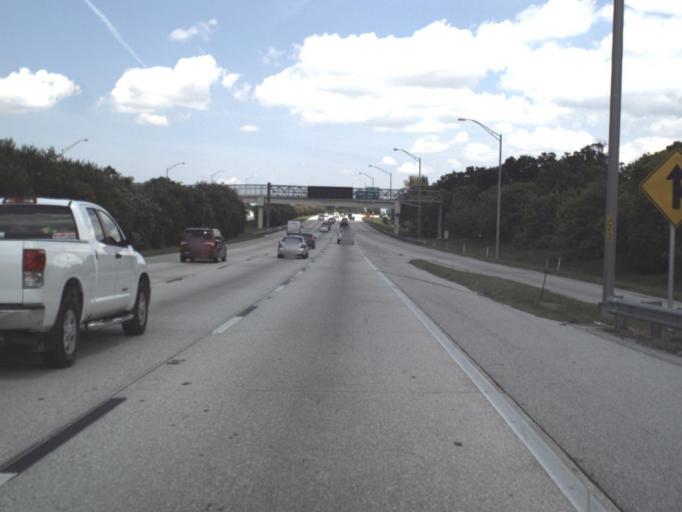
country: US
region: Florida
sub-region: Pinellas County
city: Saint Petersburg
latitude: 27.7947
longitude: -82.6608
